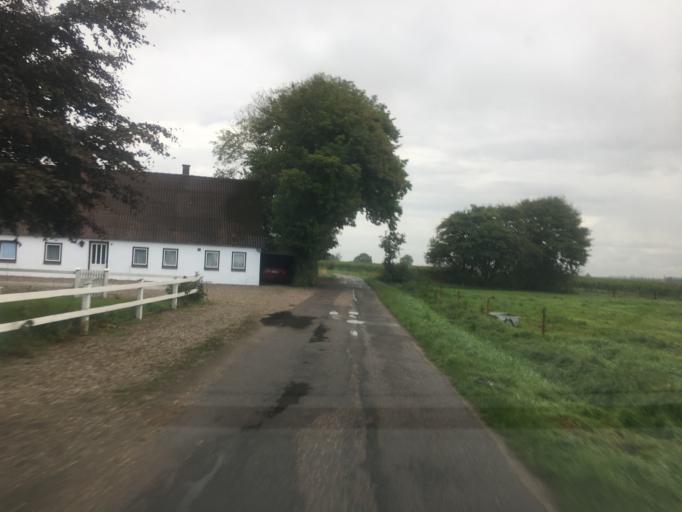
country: DK
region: South Denmark
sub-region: Tonder Kommune
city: Tonder
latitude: 54.9761
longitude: 8.9064
